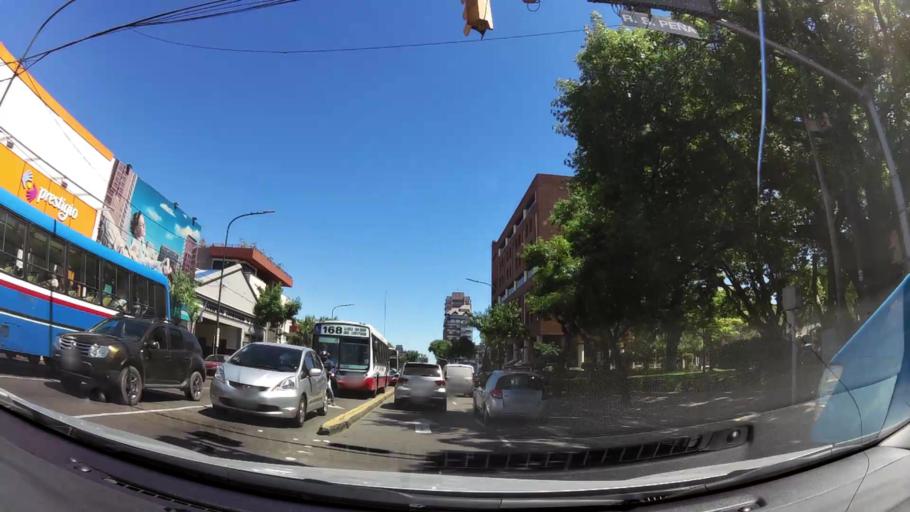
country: AR
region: Buenos Aires
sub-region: Partido de San Isidro
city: San Isidro
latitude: -34.4742
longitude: -58.5127
